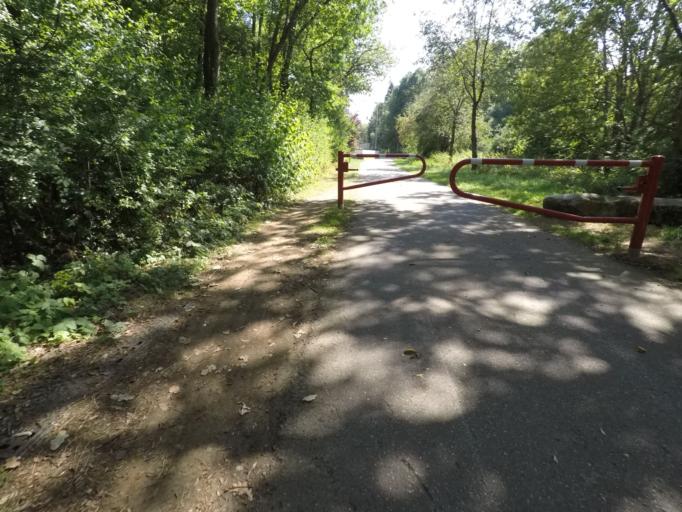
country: LU
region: Luxembourg
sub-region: Canton de Capellen
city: Clemency
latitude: 49.5981
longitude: 5.8781
